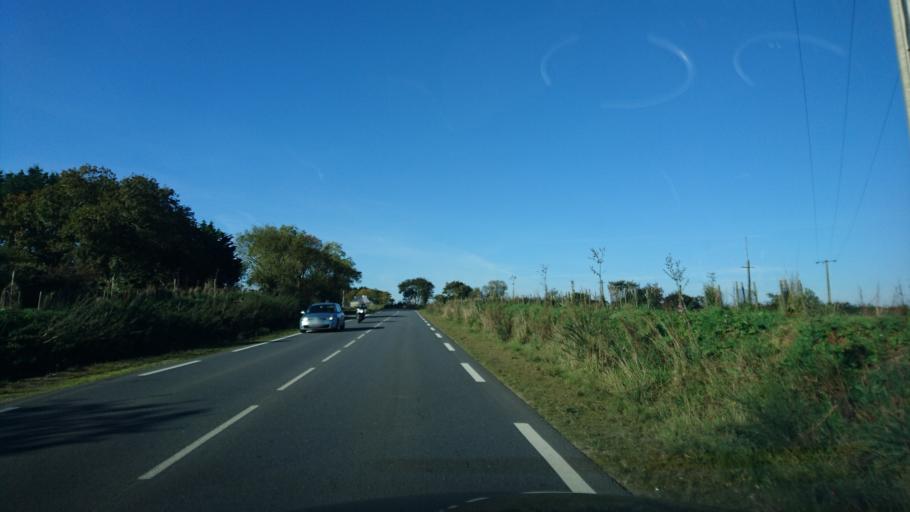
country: FR
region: Brittany
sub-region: Departement du Finistere
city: Guilers
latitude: 48.4495
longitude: -4.5424
